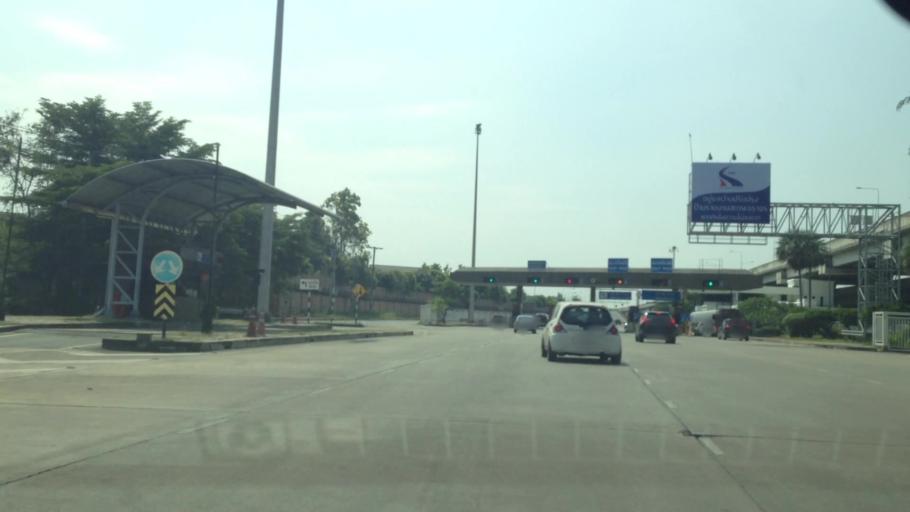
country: TH
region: Bangkok
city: Bang Khen
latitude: 13.8848
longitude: 100.6504
